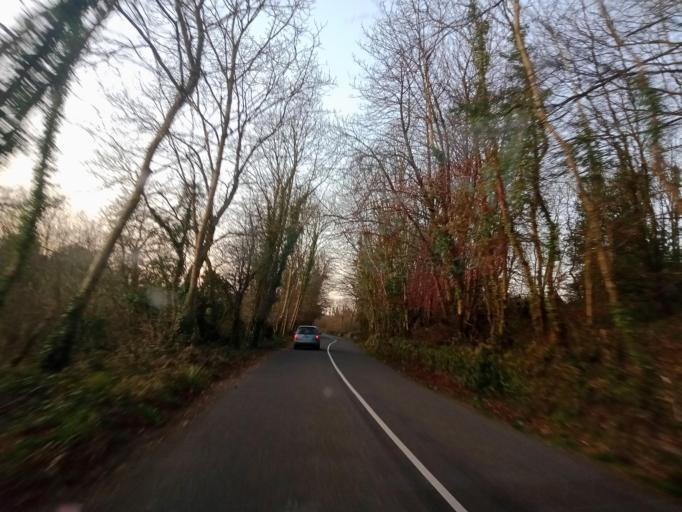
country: IE
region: Leinster
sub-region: Kilkenny
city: Castlecomer
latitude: 52.8426
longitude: -7.2588
